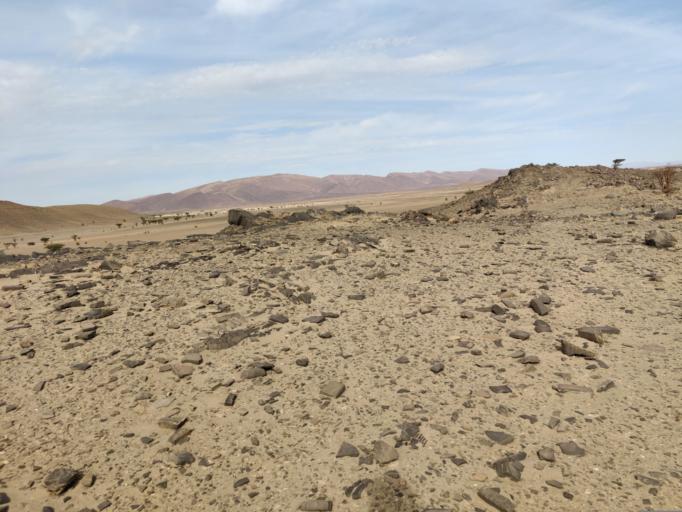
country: MA
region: Guelmim-Es Smara
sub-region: Tata
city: Tata
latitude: 29.3324
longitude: -8.1861
